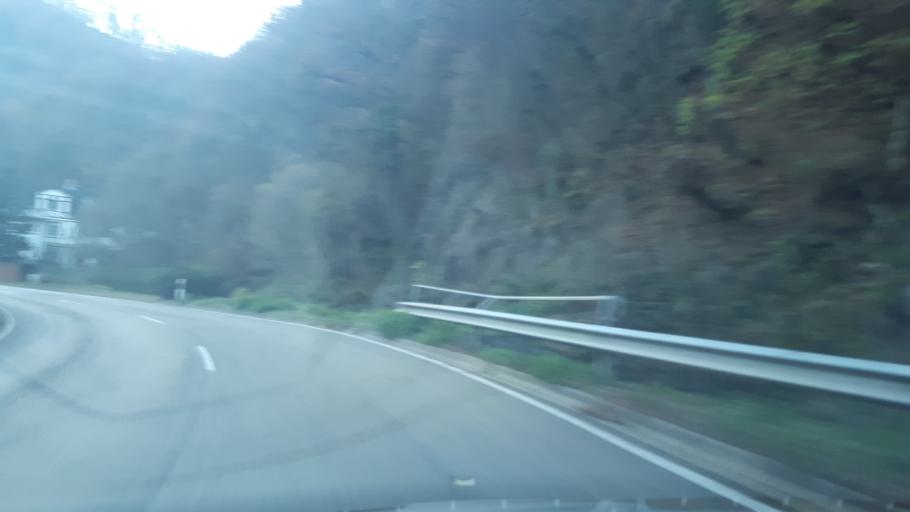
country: DE
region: Rheinland-Pfalz
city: Bad Bertrich
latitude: 50.0701
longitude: 7.0624
